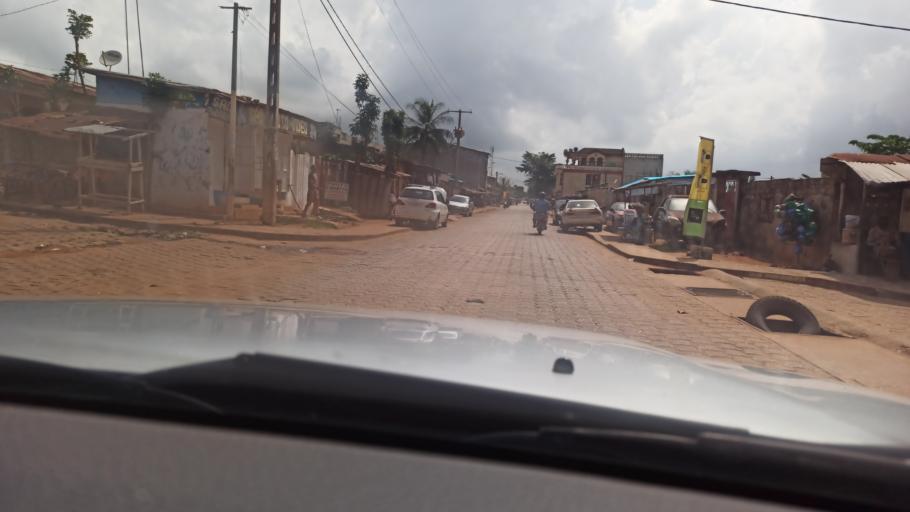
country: BJ
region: Queme
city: Porto-Novo
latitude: 6.4689
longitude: 2.6418
